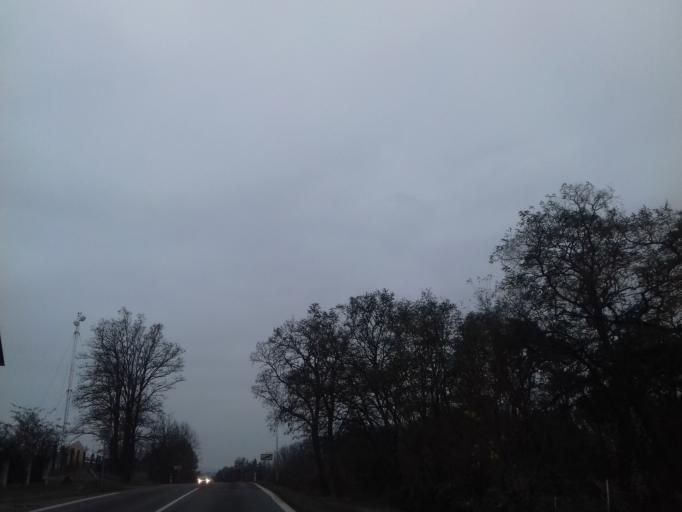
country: CZ
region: Plzensky
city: Zbuch
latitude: 49.6762
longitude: 13.2224
